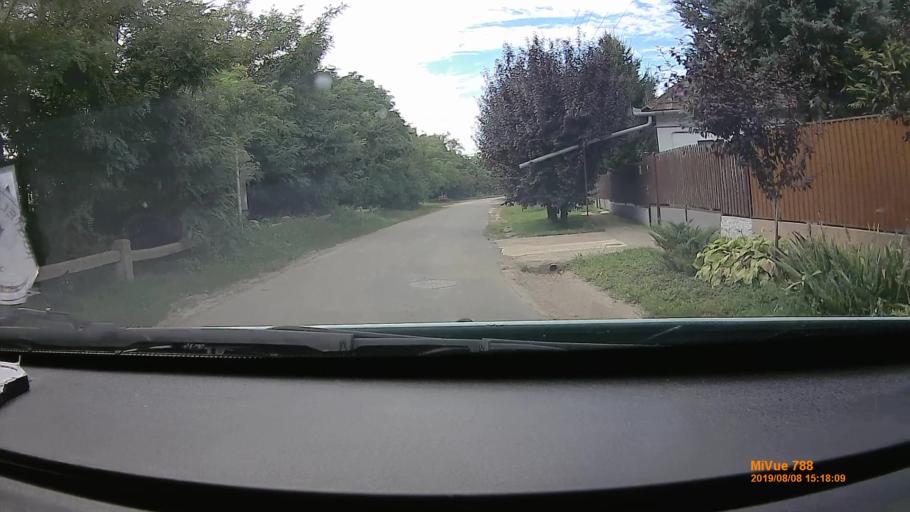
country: HU
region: Szabolcs-Szatmar-Bereg
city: Tunyogmatolcs
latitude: 47.9650
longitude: 22.4591
